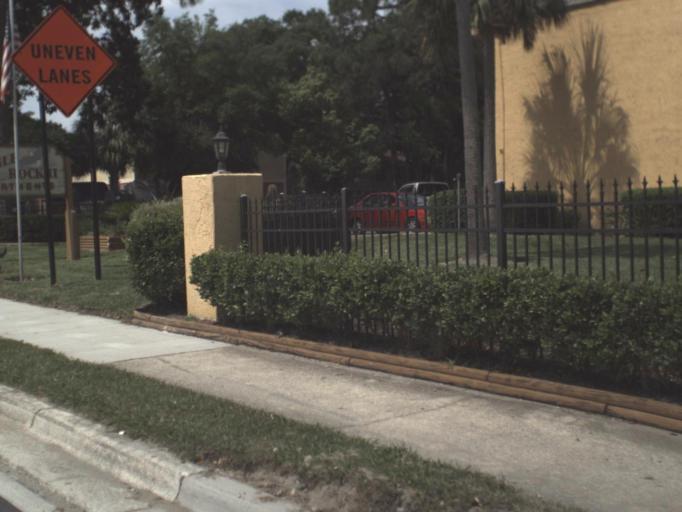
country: US
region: Florida
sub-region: Duval County
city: Jacksonville
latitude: 30.2871
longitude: -81.6025
